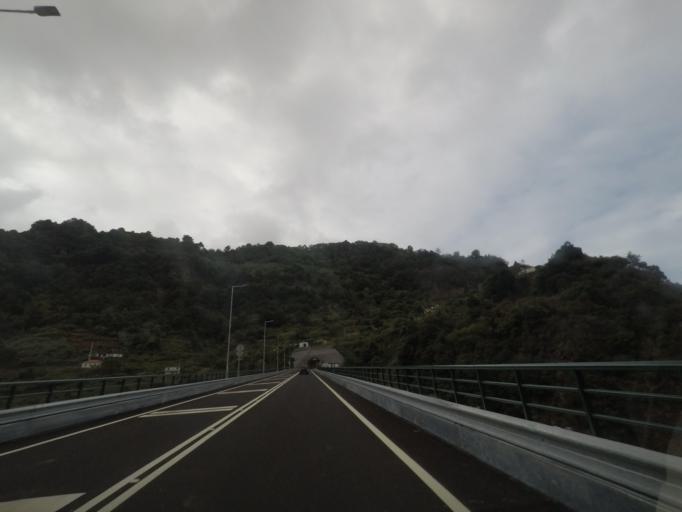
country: PT
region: Madeira
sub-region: Santana
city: Santana
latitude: 32.8157
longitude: -16.9015
